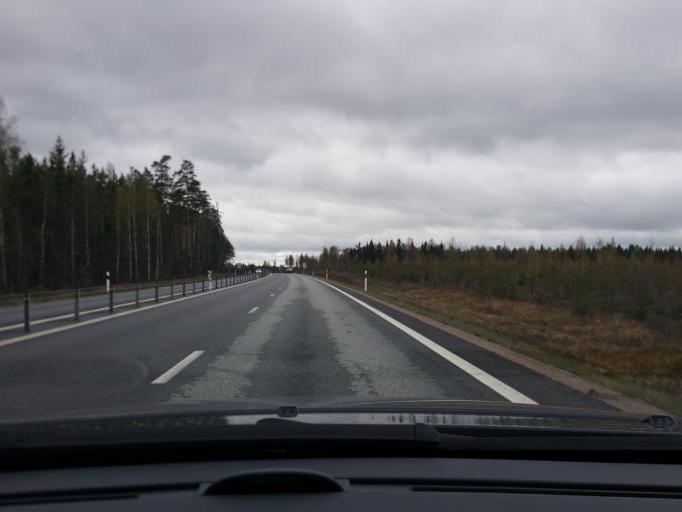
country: SE
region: Kronoberg
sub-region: Vaxjo Kommun
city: Vaexjoe
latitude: 56.9289
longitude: 14.7199
